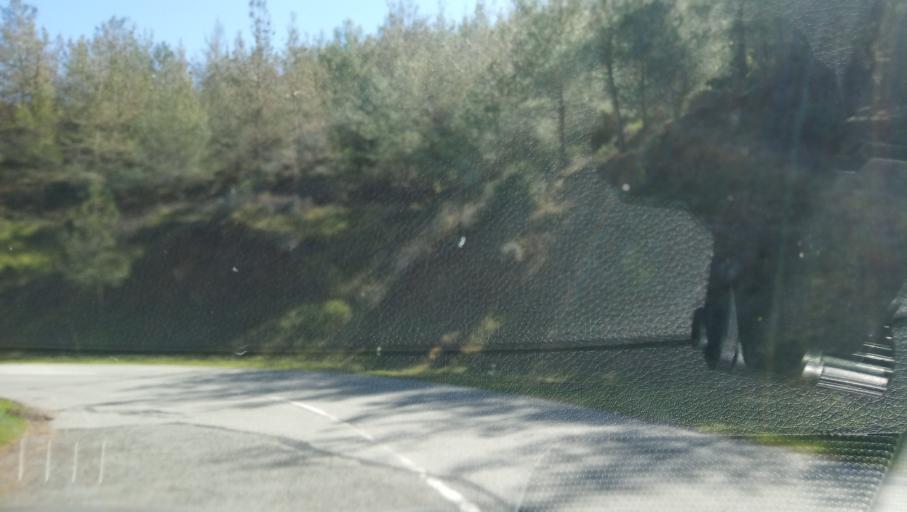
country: CY
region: Lefkosia
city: Lefka
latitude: 35.0853
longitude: 32.7849
